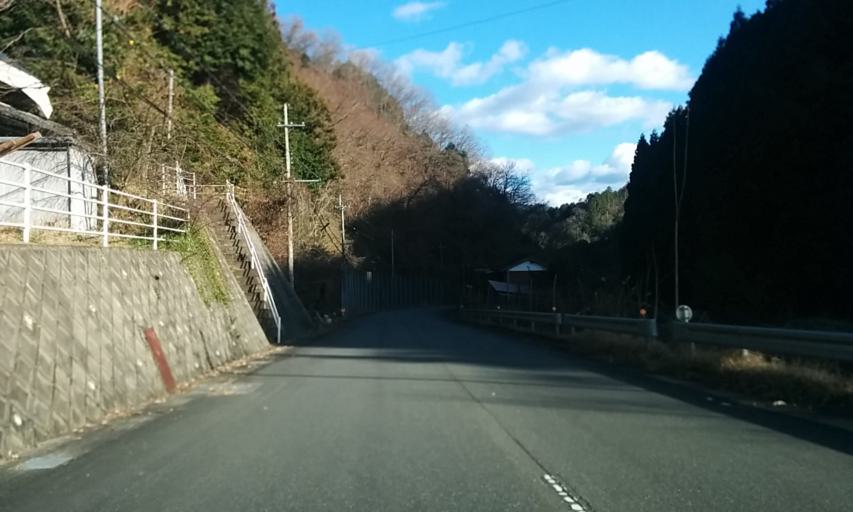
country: JP
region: Kyoto
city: Fukuchiyama
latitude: 35.2765
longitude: 135.0213
